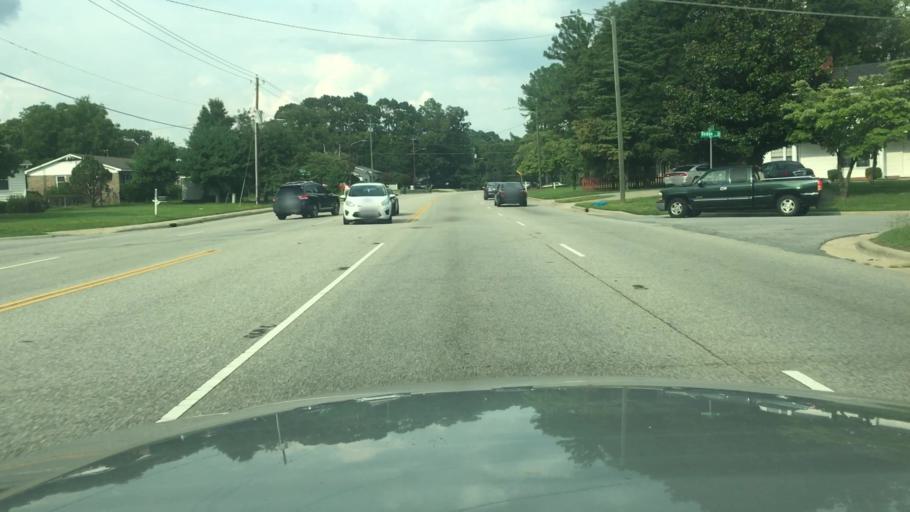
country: US
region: North Carolina
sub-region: Cumberland County
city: Fort Bragg
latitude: 35.0925
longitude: -78.9787
